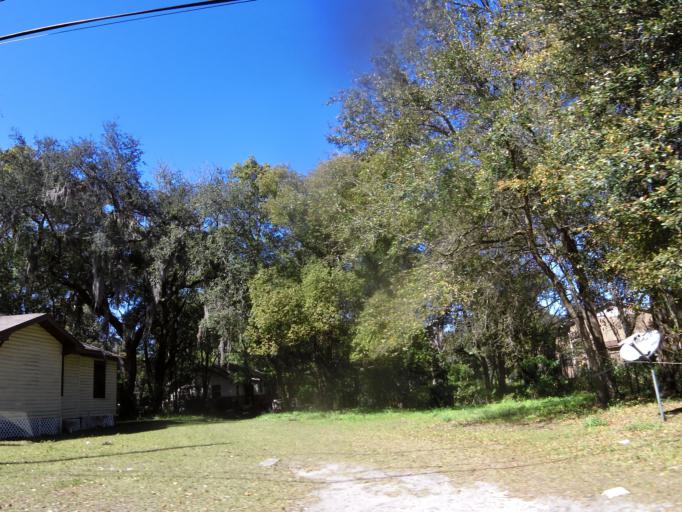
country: US
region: Florida
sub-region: Duval County
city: Jacksonville
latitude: 30.3617
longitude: -81.6443
